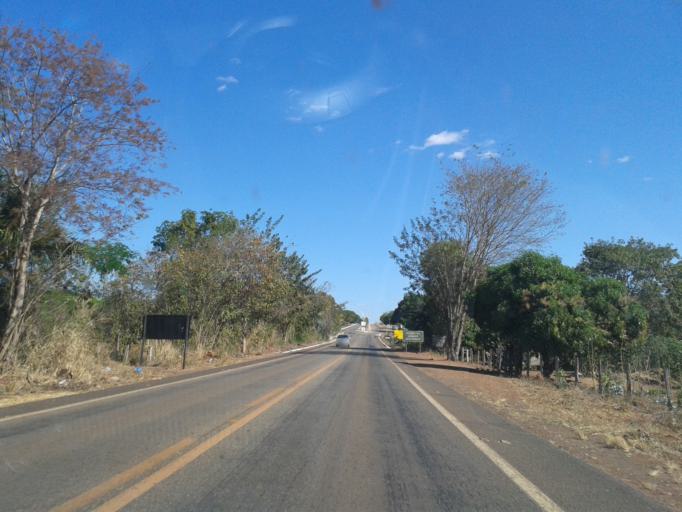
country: BR
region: Goias
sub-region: Crixas
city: Crixas
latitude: -14.0865
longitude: -50.3349
